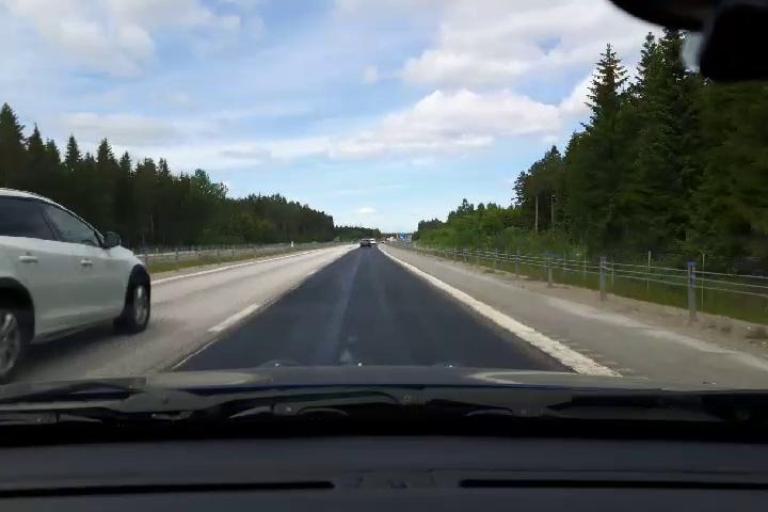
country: SE
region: Uppsala
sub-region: Alvkarleby Kommun
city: AElvkarleby
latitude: 60.4494
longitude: 17.4162
